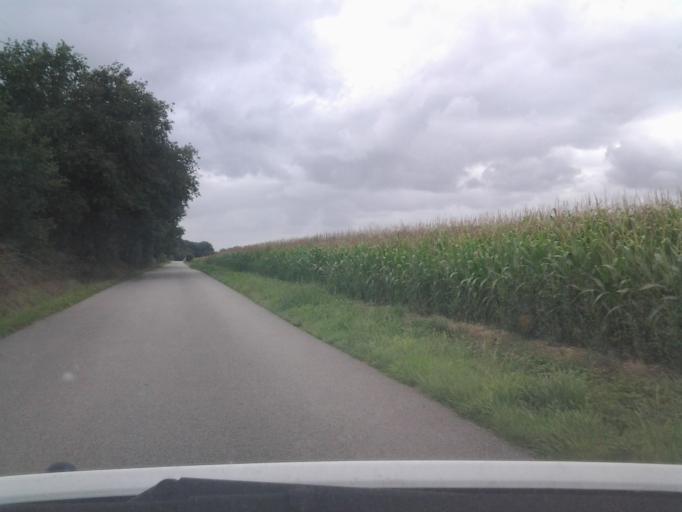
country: FR
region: Pays de la Loire
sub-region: Departement de la Vendee
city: Dompierre-sur-Yon
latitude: 46.7053
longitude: -1.3758
